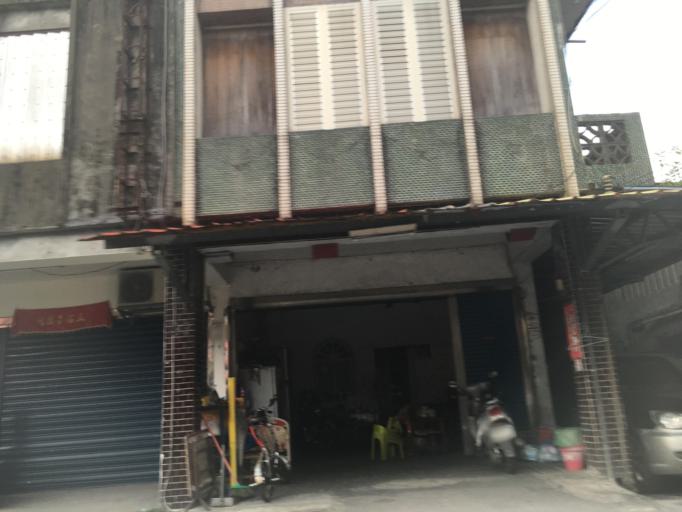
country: TW
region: Taiwan
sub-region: Yilan
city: Yilan
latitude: 24.6932
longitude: 121.7293
